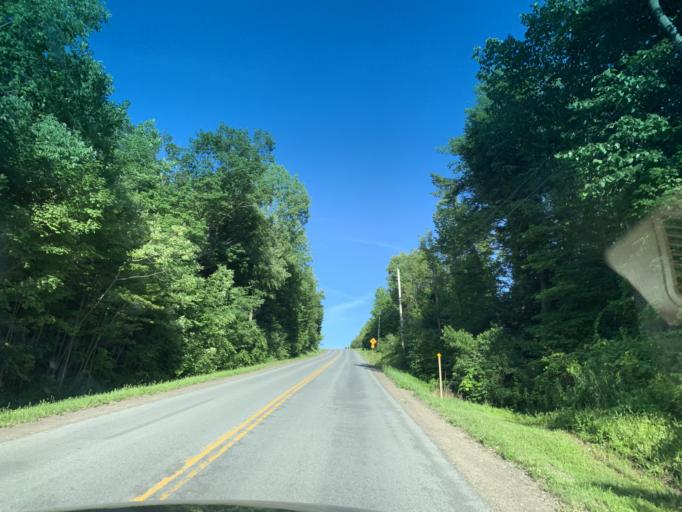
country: US
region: New York
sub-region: Oneida County
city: Clinton
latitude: 43.0554
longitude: -75.4599
